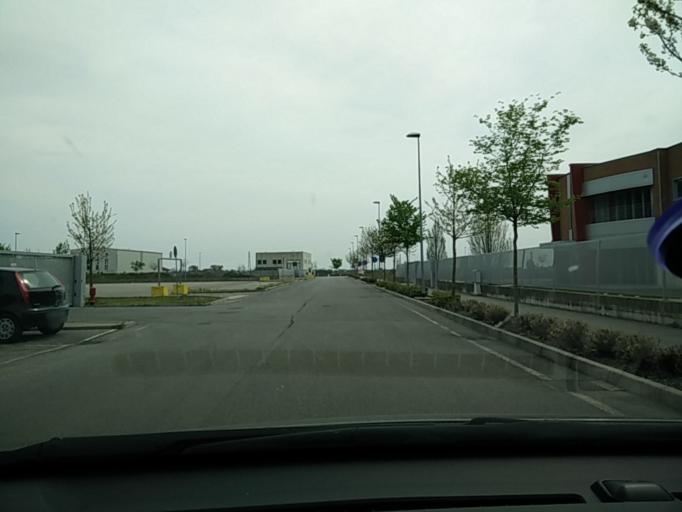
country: IT
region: Veneto
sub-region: Provincia di Venezia
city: Musile di Piave
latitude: 45.6178
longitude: 12.5347
